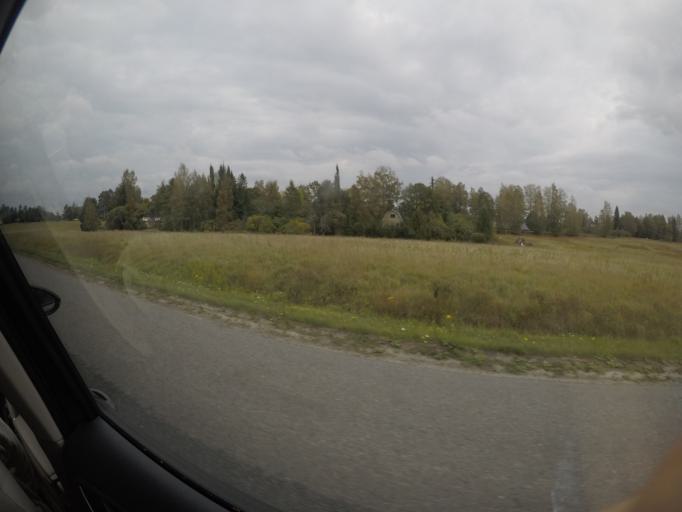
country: FI
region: Haeme
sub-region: Haemeenlinna
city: Parola
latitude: 61.0536
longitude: 24.3936
